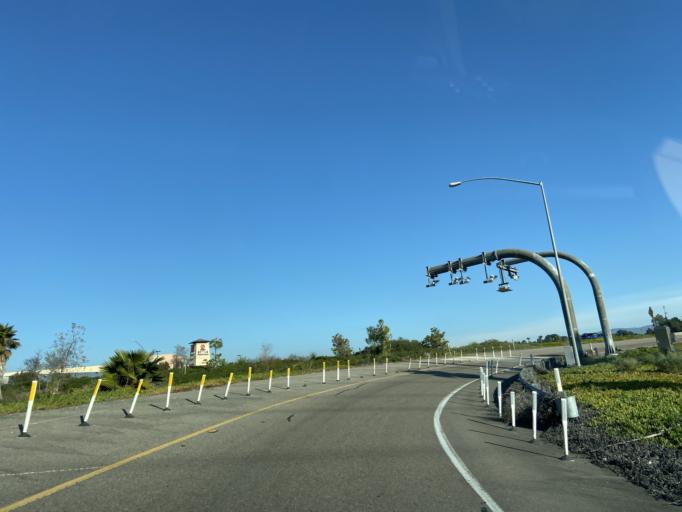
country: US
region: California
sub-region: San Diego County
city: Bonita
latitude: 32.6471
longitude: -116.9721
